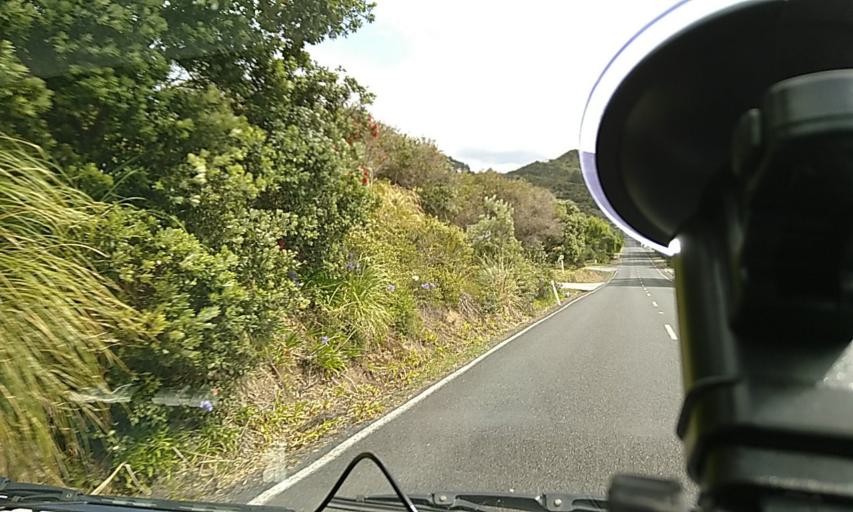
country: NZ
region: Northland
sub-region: Far North District
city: Ahipara
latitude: -35.5321
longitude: 173.3897
